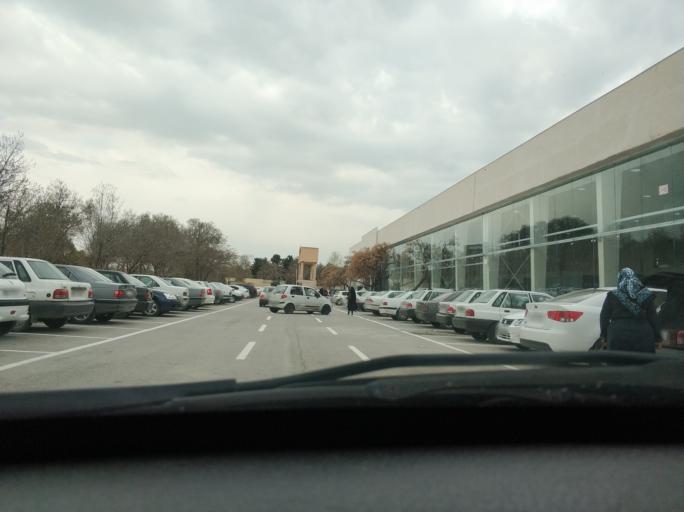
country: IR
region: Razavi Khorasan
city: Mashhad
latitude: 36.2561
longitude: 59.6098
